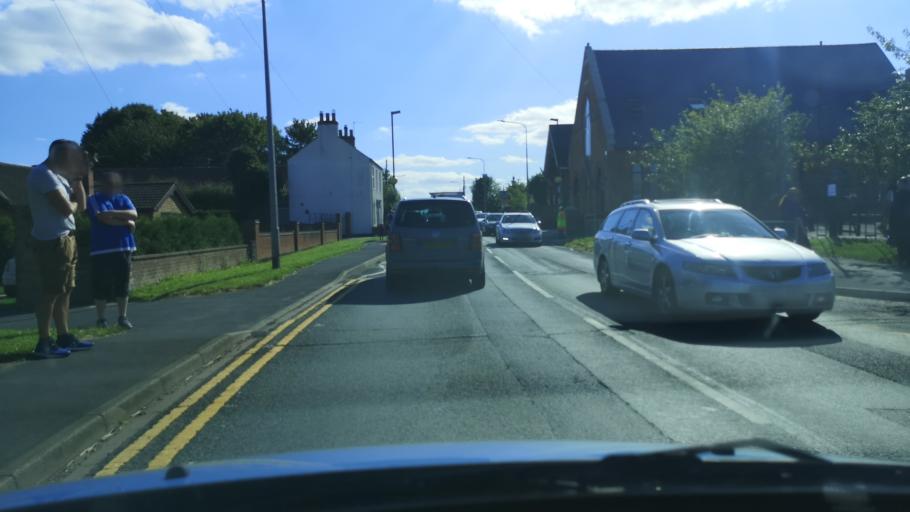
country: GB
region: England
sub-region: North Lincolnshire
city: Belton
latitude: 53.5555
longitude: -0.8155
